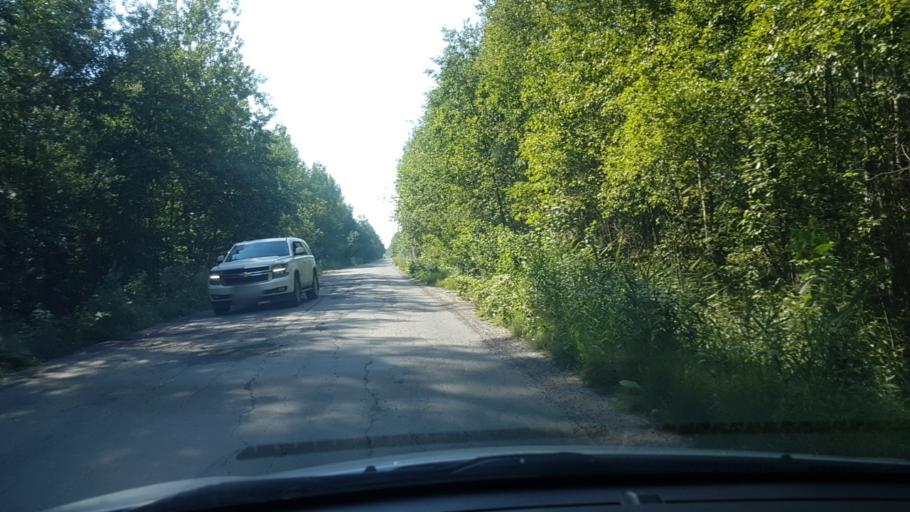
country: RU
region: Leningrad
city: Vyritsa
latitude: 59.4485
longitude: 30.3071
